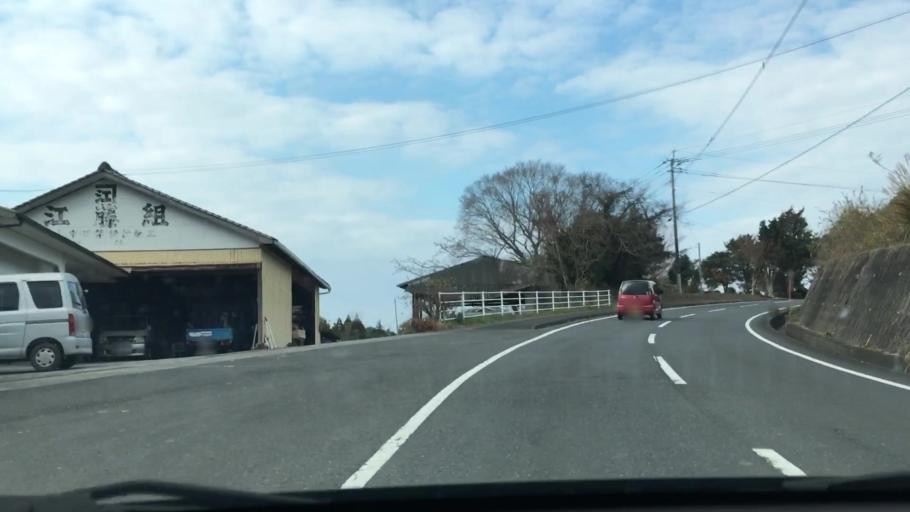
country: JP
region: Miyazaki
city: Kushima
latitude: 31.5020
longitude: 131.2388
